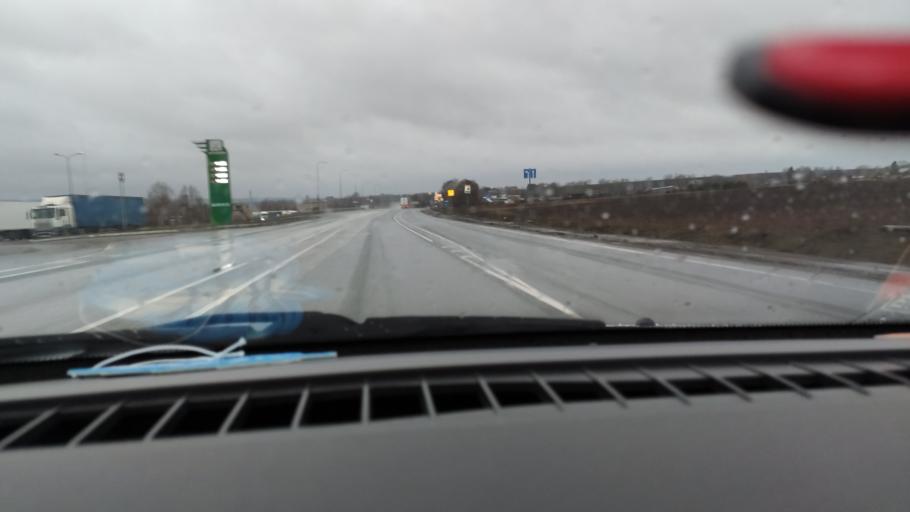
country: RU
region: Tatarstan
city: Mendeleyevsk
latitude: 56.0343
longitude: 52.3816
